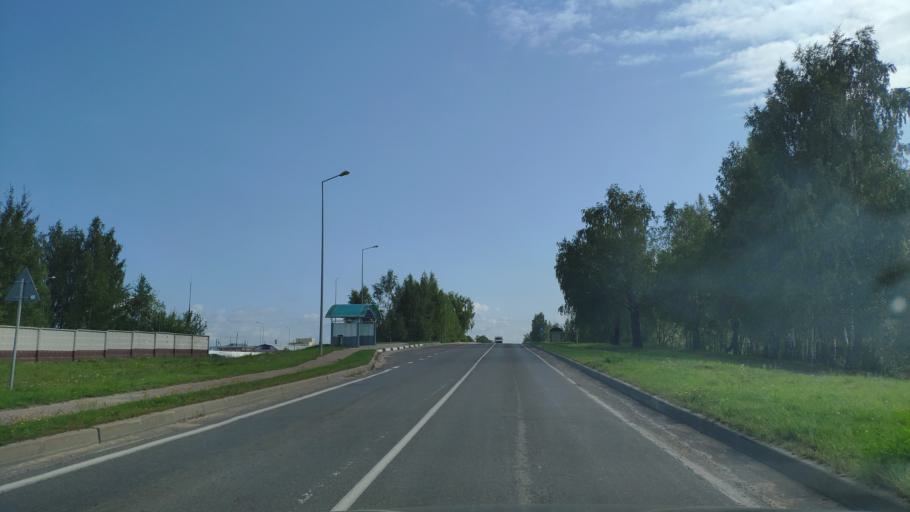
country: BY
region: Minsk
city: Zaslawye
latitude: 53.9891
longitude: 27.2608
